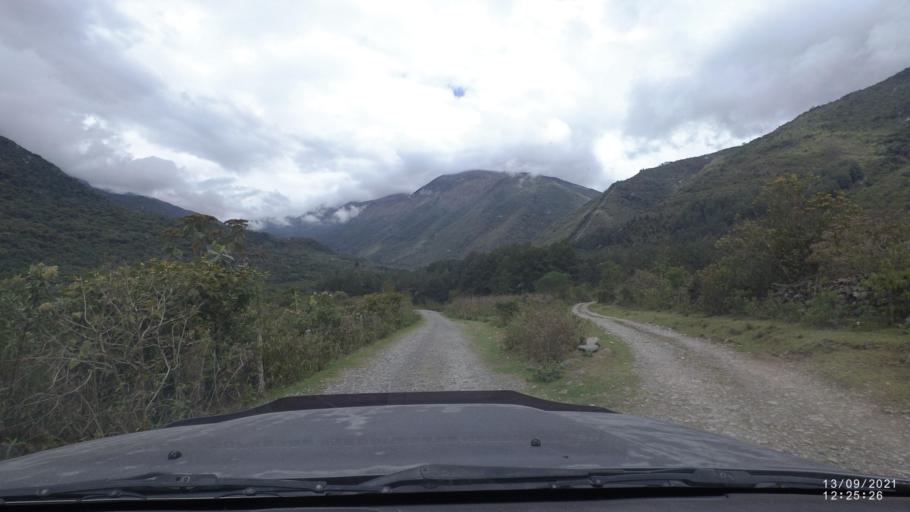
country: BO
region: Cochabamba
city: Colomi
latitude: -17.2512
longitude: -65.8167
